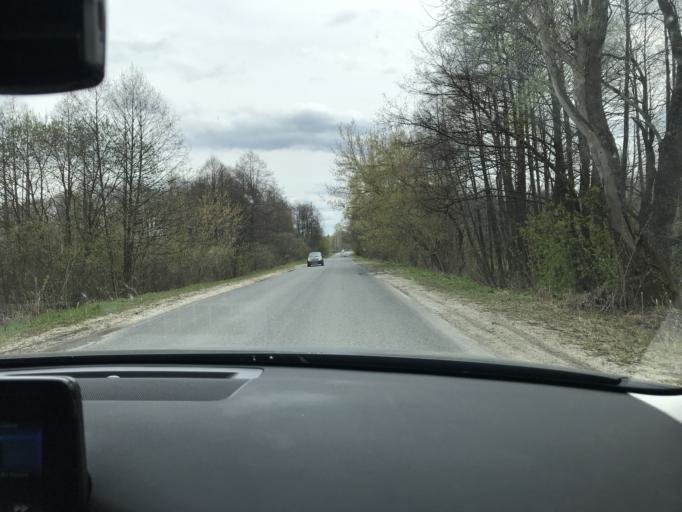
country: RU
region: Mordoviya
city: Zubova Polyana
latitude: 54.0339
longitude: 42.8322
